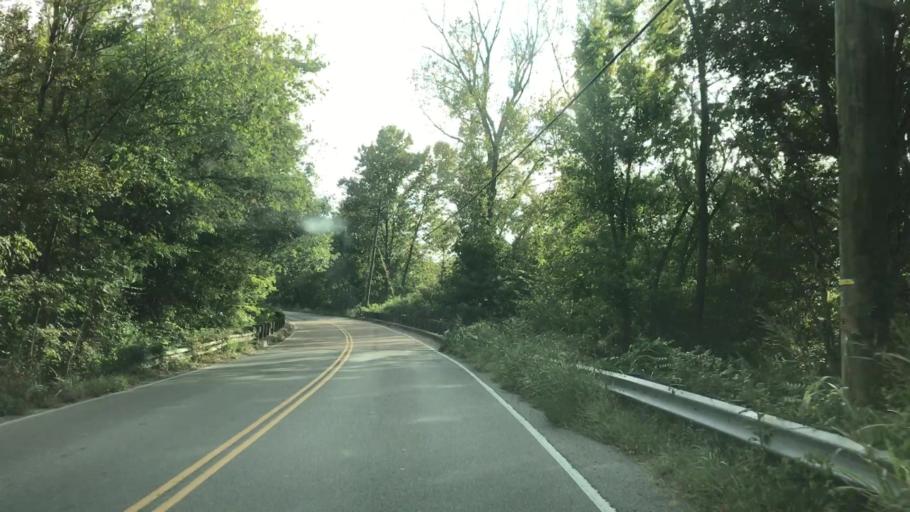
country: US
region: Tennessee
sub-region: Davidson County
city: Forest Hills
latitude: 36.0493
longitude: -86.9034
